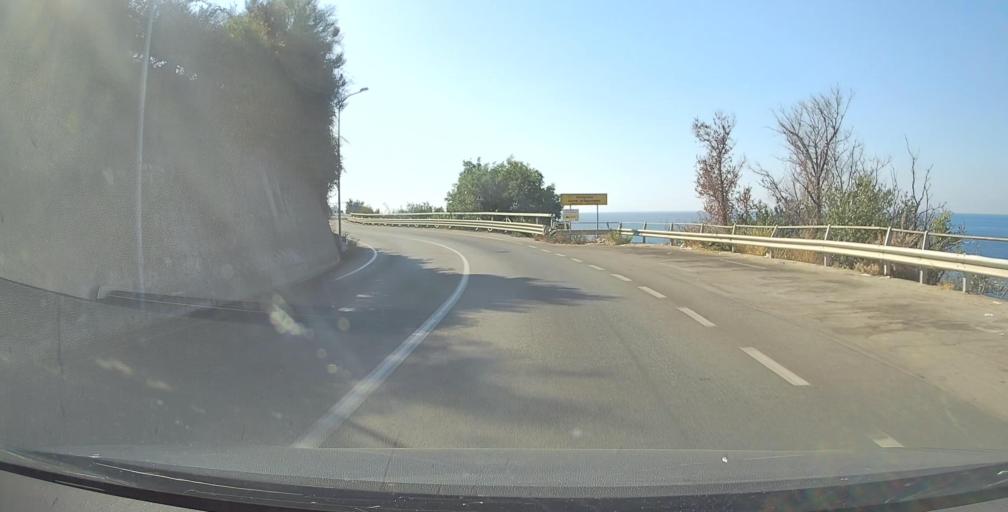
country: IT
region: Sicily
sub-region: Messina
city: Naso
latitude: 38.1536
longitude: 14.7799
